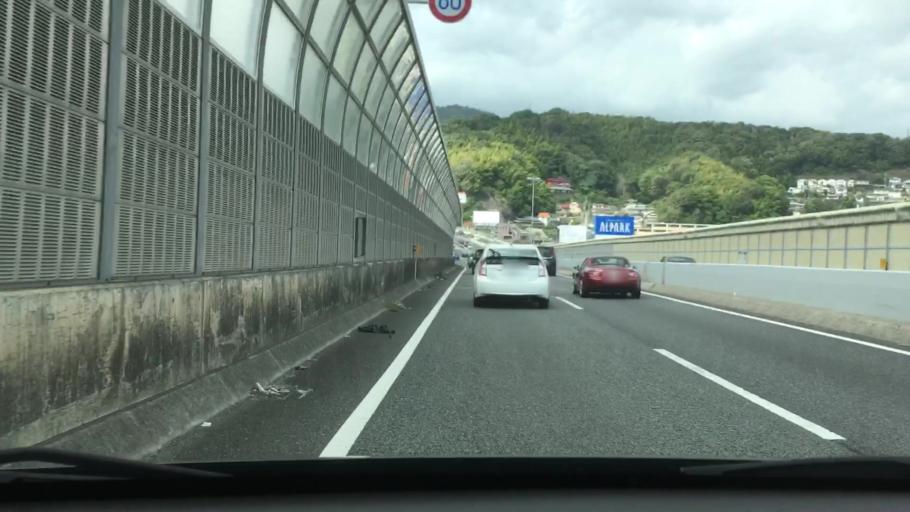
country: JP
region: Hiroshima
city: Hiroshima-shi
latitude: 34.3910
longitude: 132.4239
